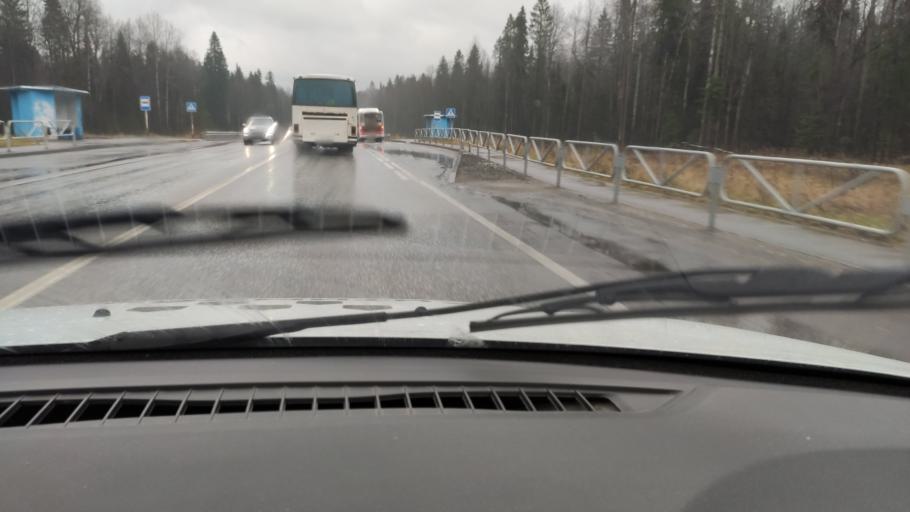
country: RU
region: Perm
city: Novyye Lyady
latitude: 58.0491
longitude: 56.5606
